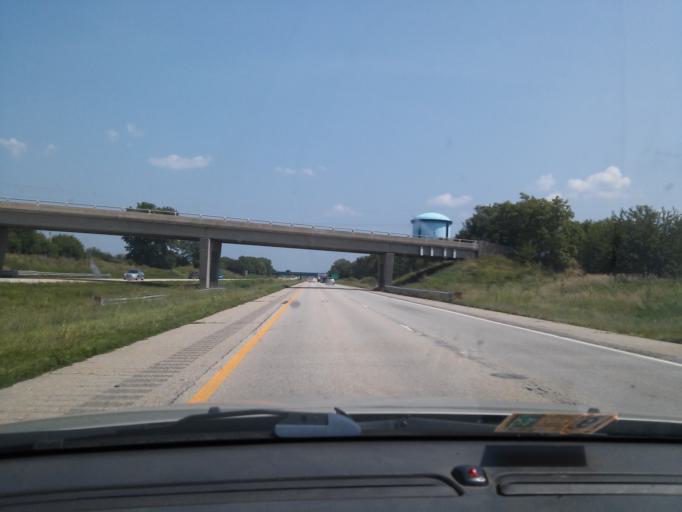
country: US
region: Illinois
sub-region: Sangamon County
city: Jerome
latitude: 39.7470
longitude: -89.7206
